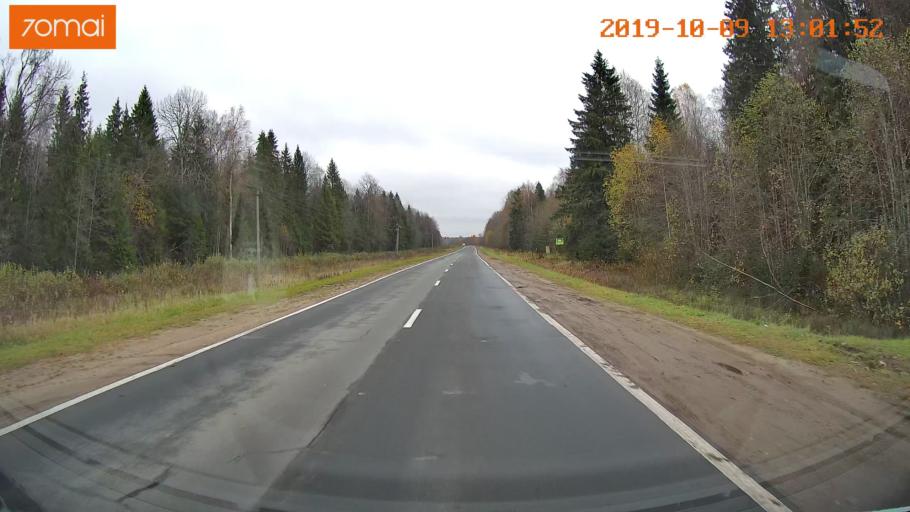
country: RU
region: Jaroslavl
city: Prechistoye
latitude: 58.3655
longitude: 40.4914
